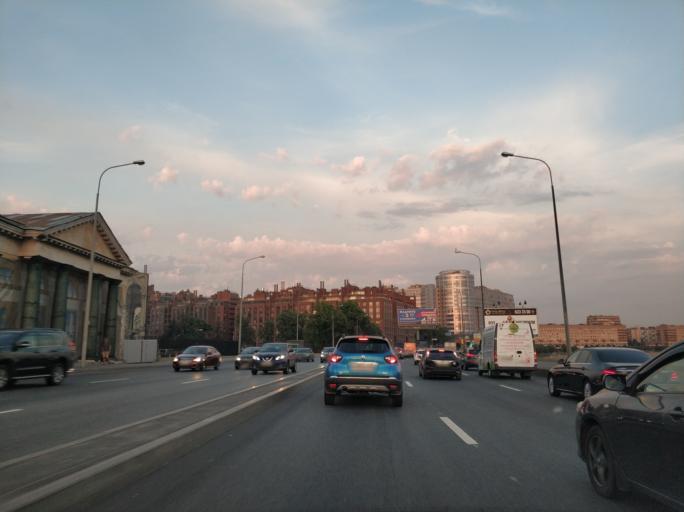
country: RU
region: Leningrad
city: Finlyandskiy
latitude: 59.9585
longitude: 30.4001
